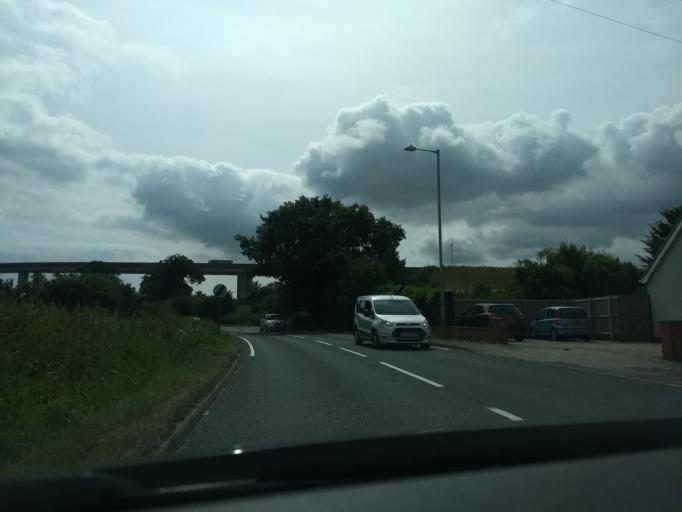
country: GB
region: England
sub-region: Suffolk
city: Ipswich
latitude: 52.0295
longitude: 1.1541
